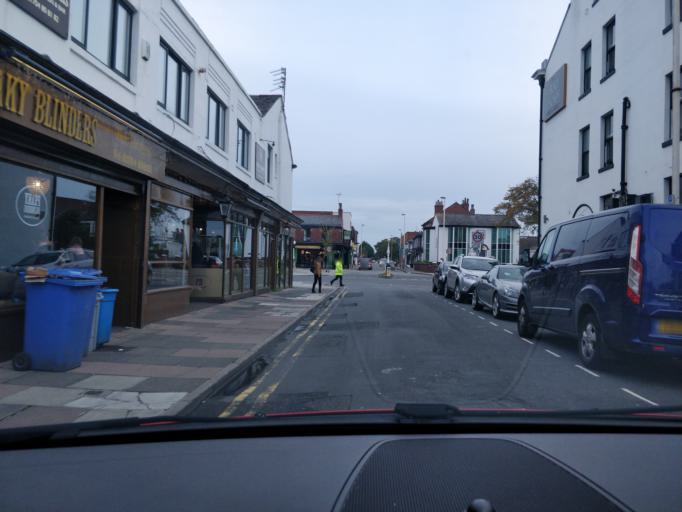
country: GB
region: England
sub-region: Sefton
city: Southport
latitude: 53.6515
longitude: -3.0010
